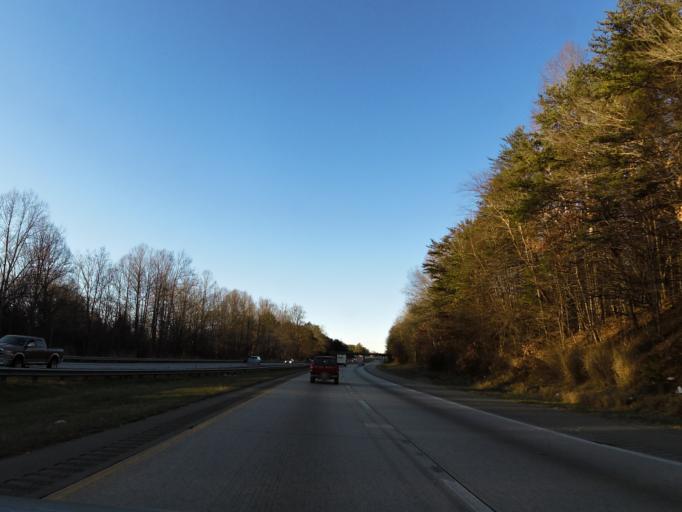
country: US
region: North Carolina
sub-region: Henderson County
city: Balfour
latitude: 35.3502
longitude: -82.4535
